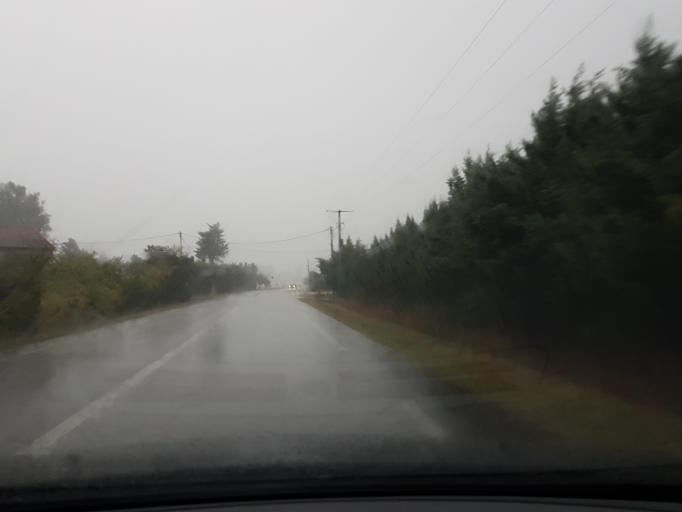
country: FR
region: Provence-Alpes-Cote d'Azur
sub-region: Departement du Vaucluse
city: Pernes-les-Fontaines
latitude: 44.0045
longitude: 5.0189
